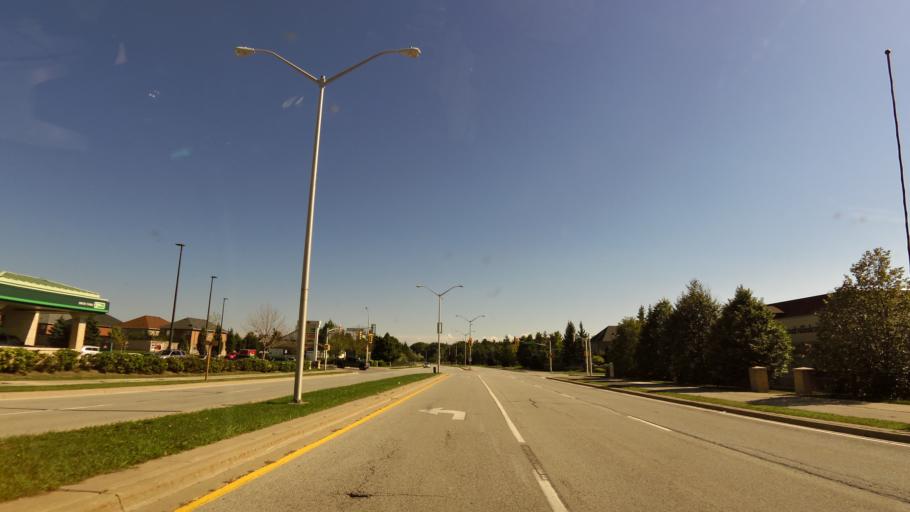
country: CA
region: Ontario
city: Oakville
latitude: 43.4636
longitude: -79.7436
